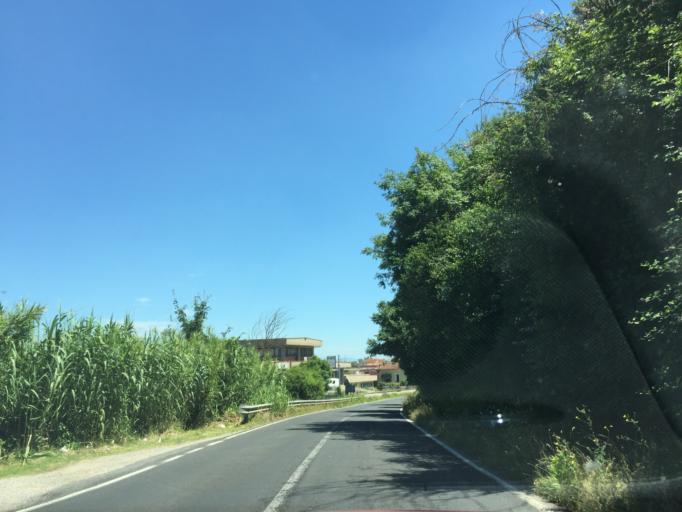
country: IT
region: Tuscany
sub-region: Province of Pisa
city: San Miniato
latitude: 43.6876
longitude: 10.7845
